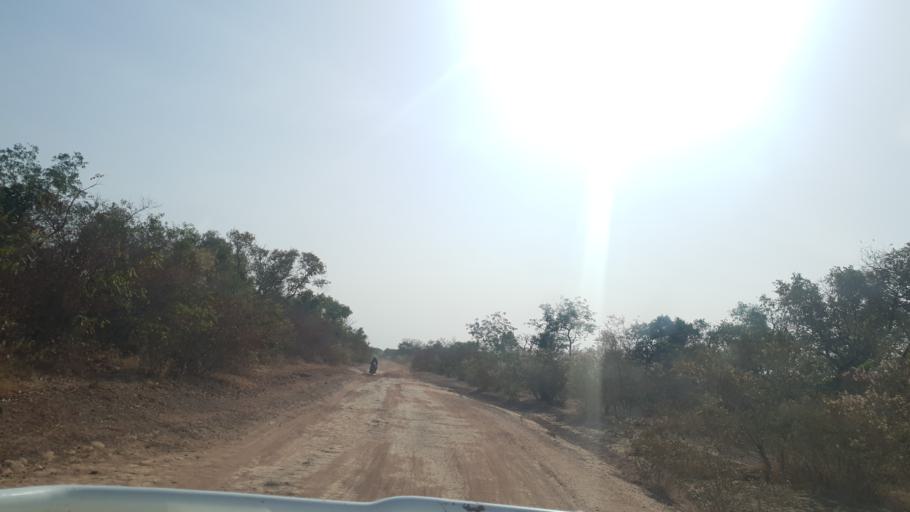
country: ML
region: Koulikoro
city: Dioila
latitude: 12.7106
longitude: -6.7865
